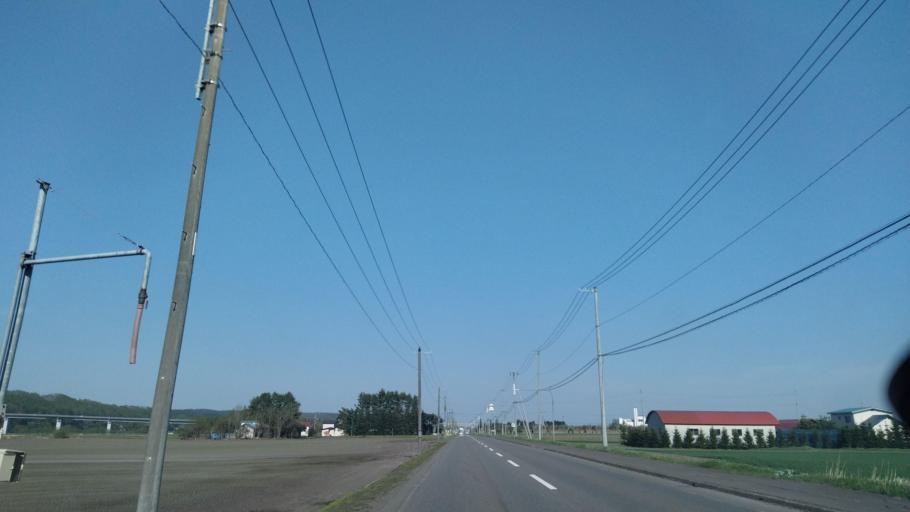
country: JP
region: Hokkaido
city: Obihiro
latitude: 42.9444
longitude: 143.0964
